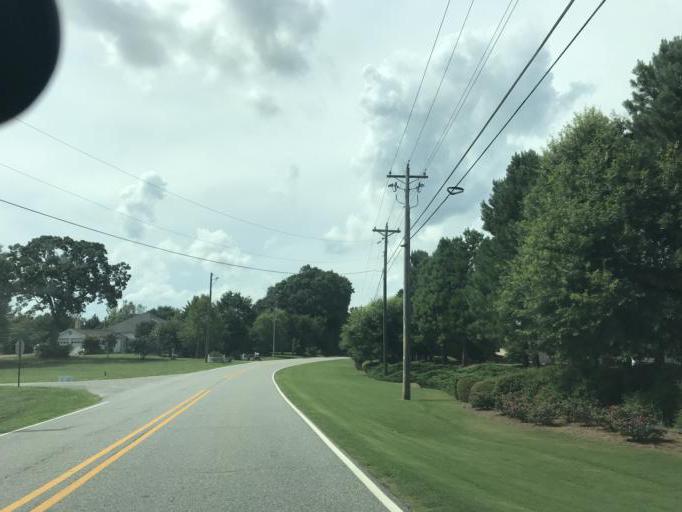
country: US
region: Georgia
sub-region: Forsyth County
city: Cumming
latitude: 34.2336
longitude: -84.2445
